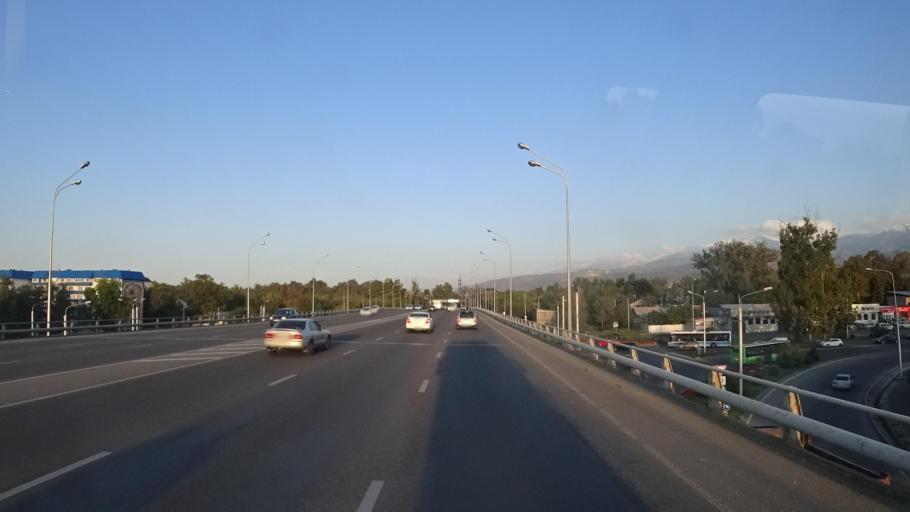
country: KZ
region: Almaty Qalasy
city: Almaty
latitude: 43.2930
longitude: 76.9392
